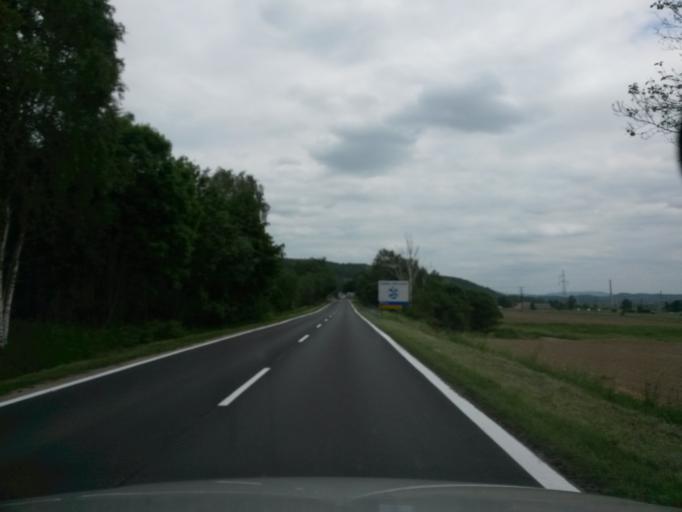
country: PL
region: Lower Silesian Voivodeship
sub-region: Jelenia Gora
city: Cieplice Slaskie Zdroj
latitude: 50.8905
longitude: 15.6699
